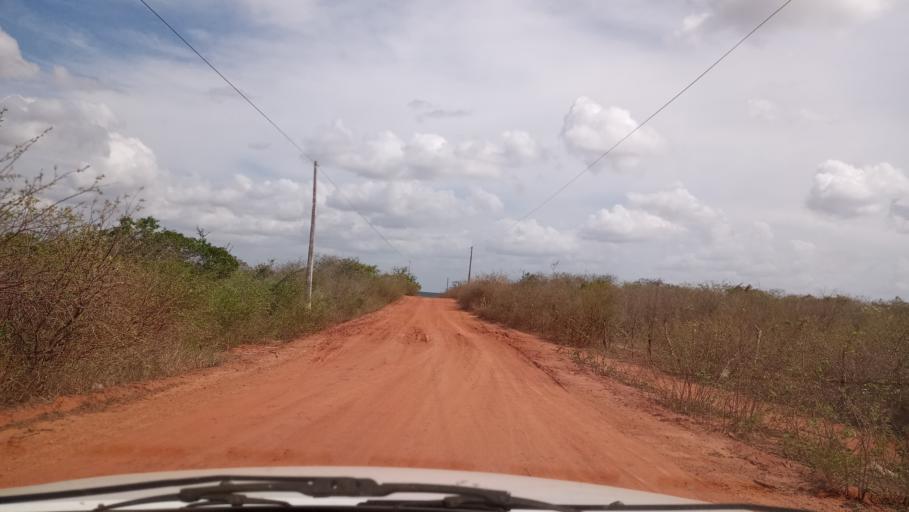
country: BR
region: Rio Grande do Norte
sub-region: Joao Camara
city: Joao Camara
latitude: -5.4587
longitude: -35.8376
